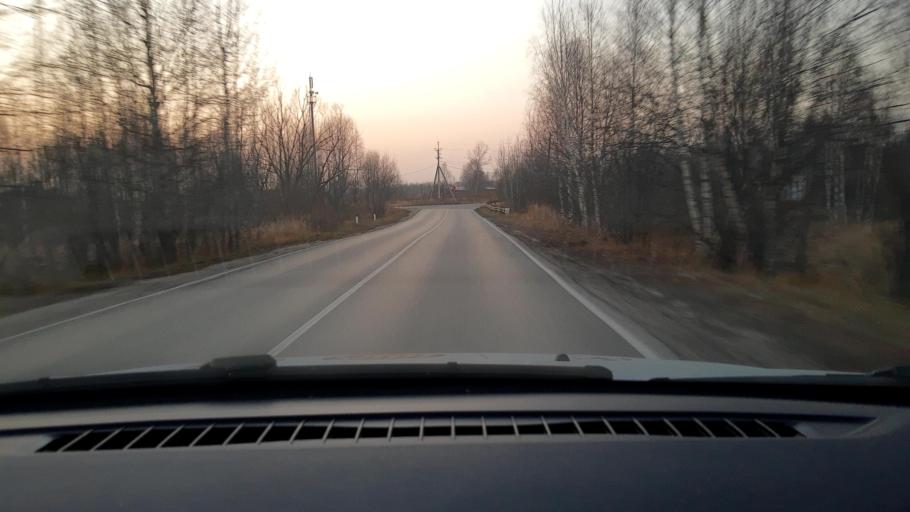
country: RU
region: Nizjnij Novgorod
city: Neklyudovo
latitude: 56.4758
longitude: 43.8775
